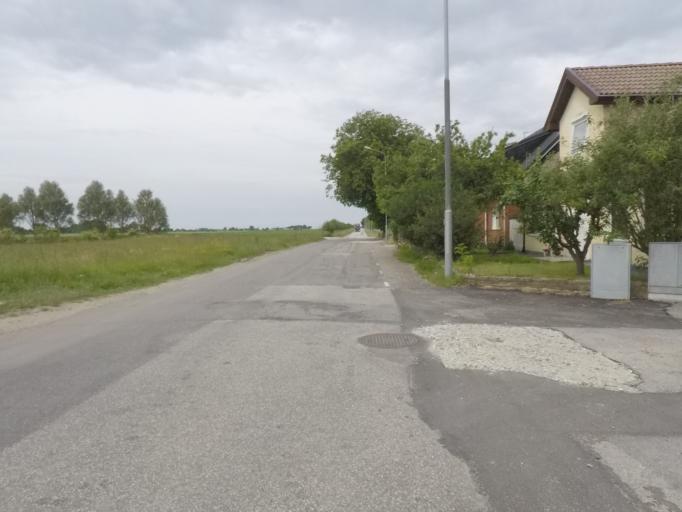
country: SE
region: Skane
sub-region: Malmo
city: Tygelsjo
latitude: 55.5163
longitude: 12.9939
